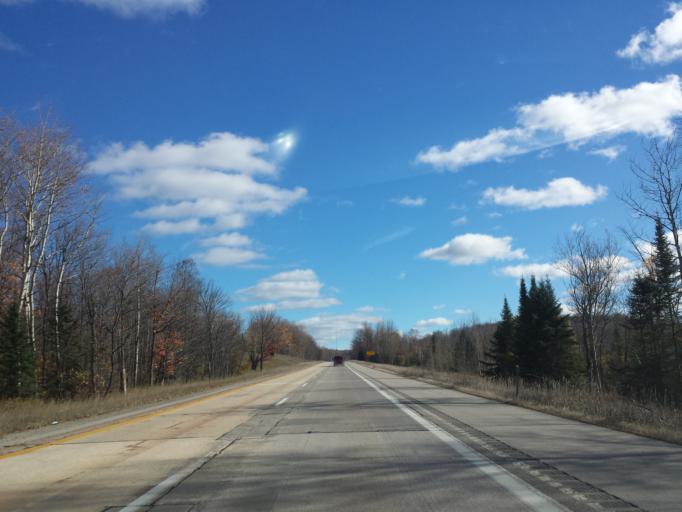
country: US
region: Michigan
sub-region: Cheboygan County
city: Cheboygan
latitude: 45.6652
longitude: -84.6485
